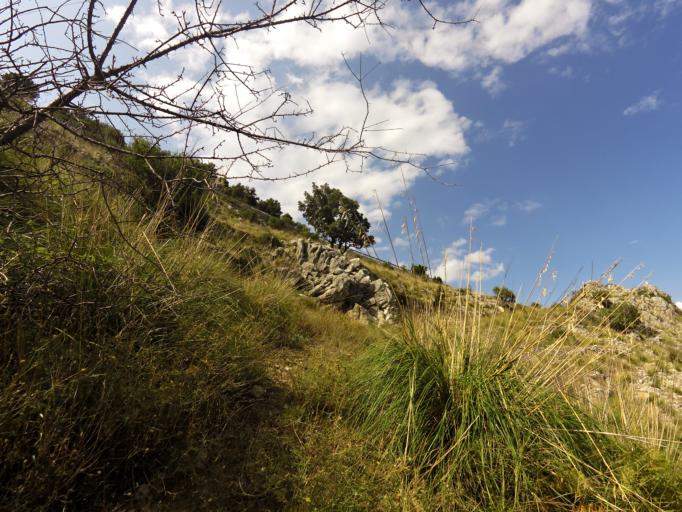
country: IT
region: Calabria
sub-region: Provincia di Reggio Calabria
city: Pazzano
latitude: 38.4653
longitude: 16.4417
